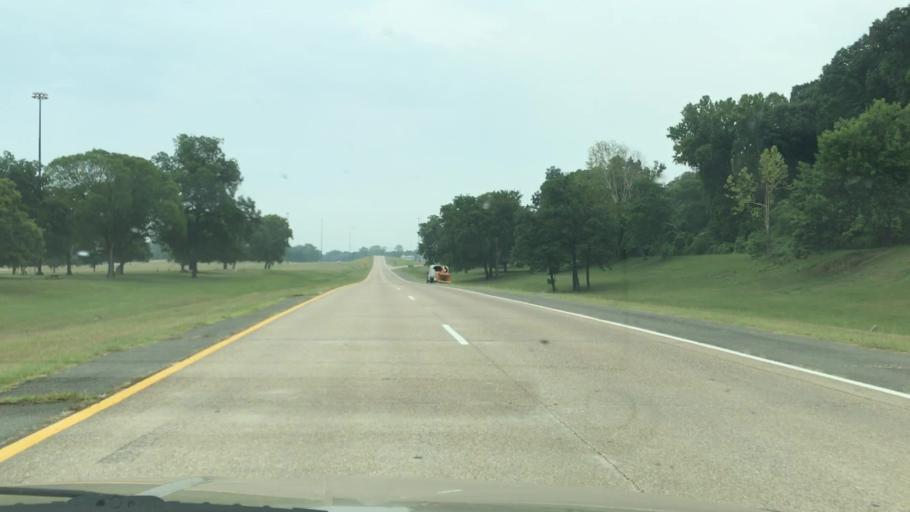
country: US
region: Louisiana
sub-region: Bossier Parish
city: Bossier City
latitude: 32.5049
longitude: -93.7212
